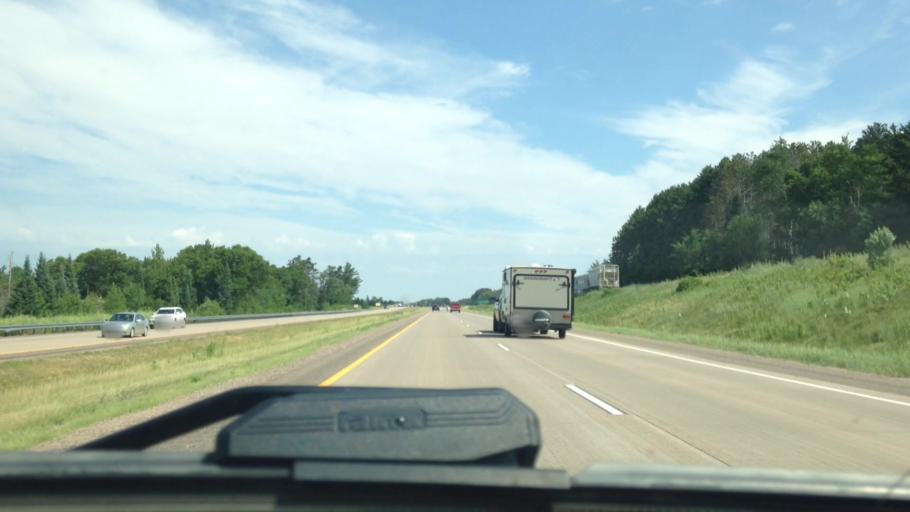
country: US
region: Wisconsin
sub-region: Washburn County
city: Spooner
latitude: 45.8739
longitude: -91.8298
